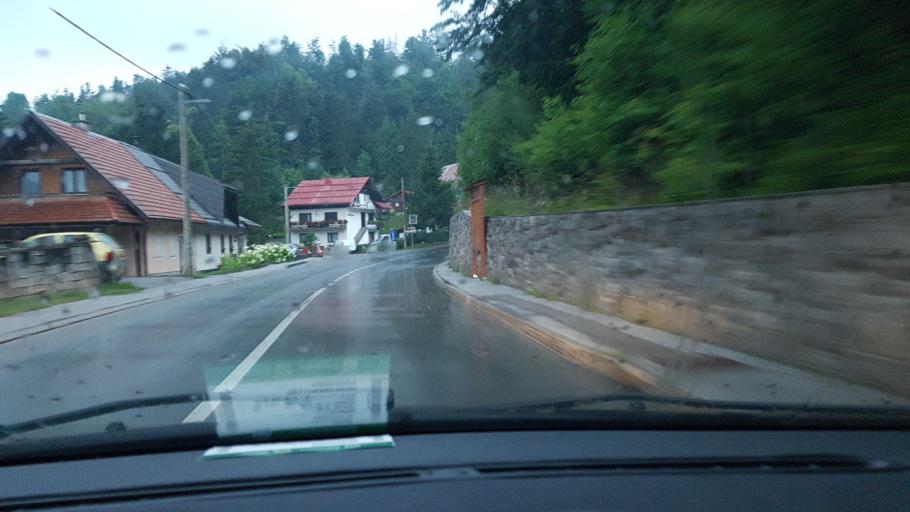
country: HR
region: Primorsko-Goranska
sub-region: Grad Delnice
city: Delnice
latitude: 45.3612
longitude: 14.7254
